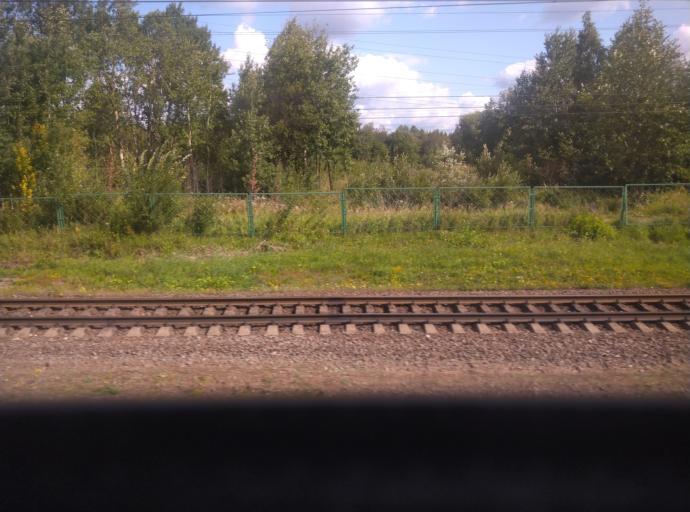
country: RU
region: St.-Petersburg
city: Kolpino
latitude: 59.7635
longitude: 30.5757
